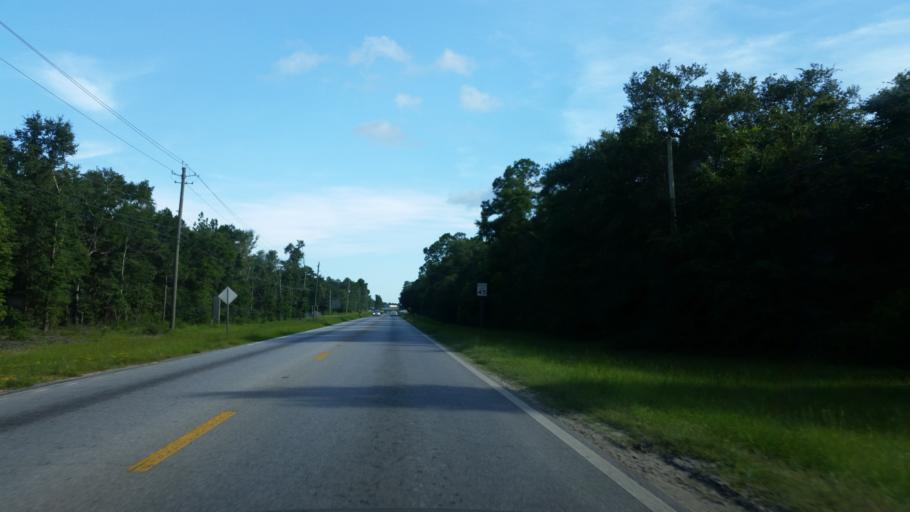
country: US
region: Florida
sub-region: Santa Rosa County
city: Bagdad
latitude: 30.5795
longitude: -87.0313
